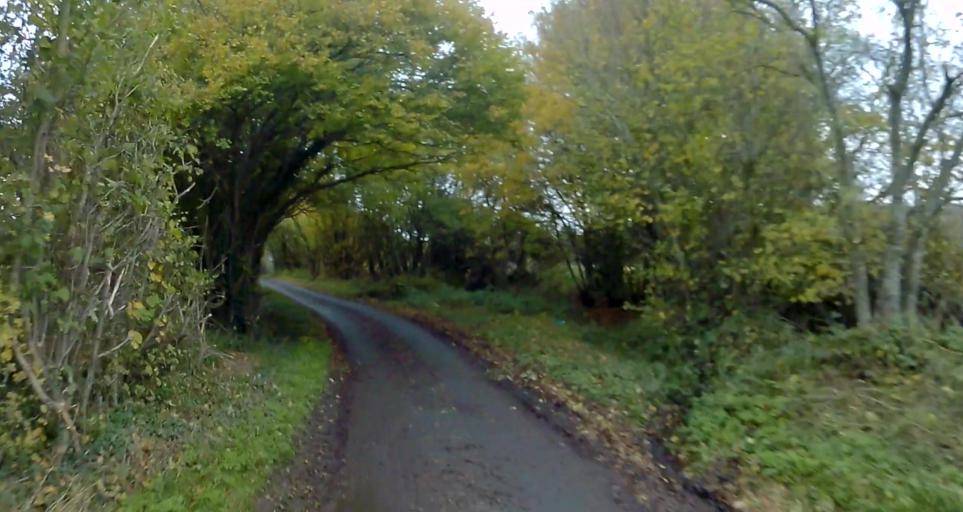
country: GB
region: England
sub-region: Hampshire
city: Odiham
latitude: 51.2452
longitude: -0.9027
